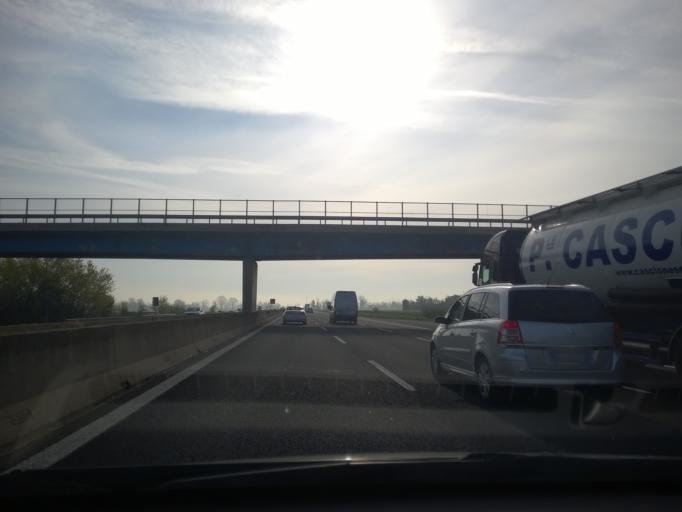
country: IT
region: Emilia-Romagna
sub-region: Provincia di Bologna
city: Toscanella
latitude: 44.4133
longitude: 11.6430
